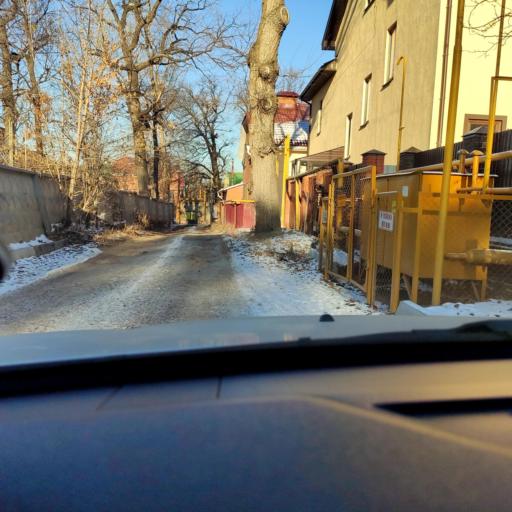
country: RU
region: Samara
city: Samara
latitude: 53.2600
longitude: 50.1982
